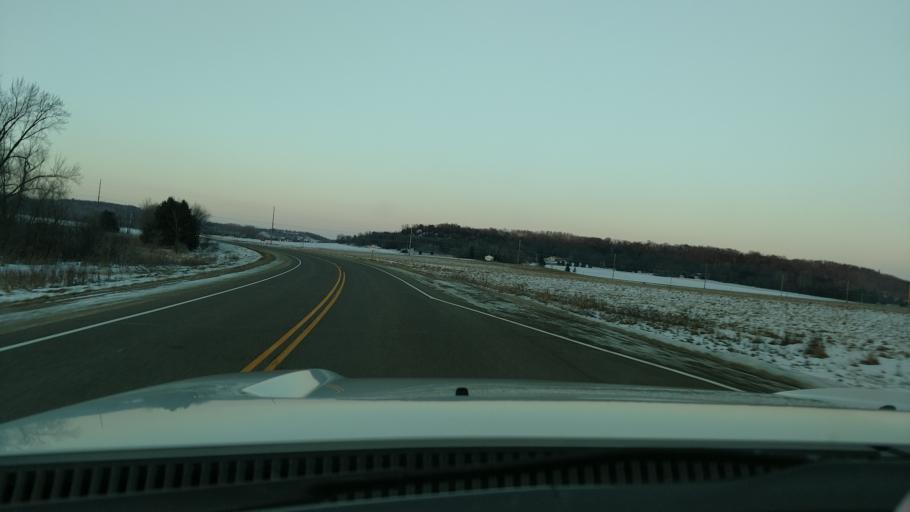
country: US
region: Wisconsin
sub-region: Saint Croix County
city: Roberts
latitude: 44.9089
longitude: -92.5586
